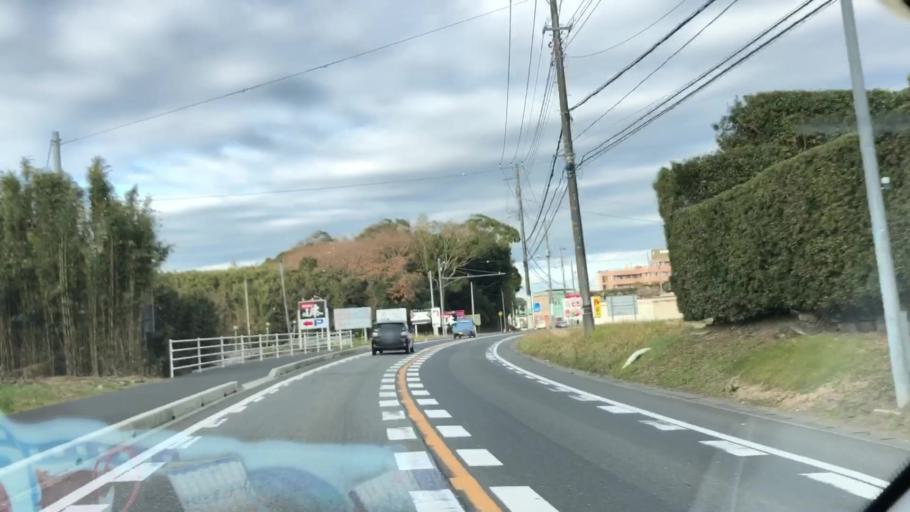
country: JP
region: Chiba
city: Tateyama
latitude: 34.9987
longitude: 139.8953
